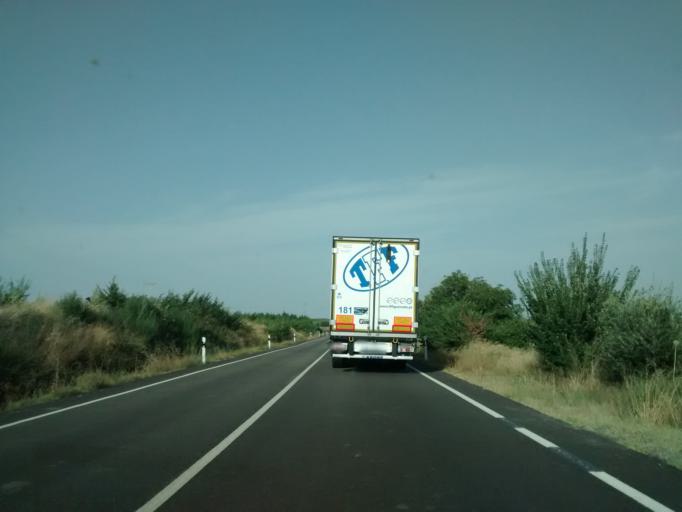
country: ES
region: Aragon
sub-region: Provincia de Zaragoza
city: Malejan
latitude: 41.8290
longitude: -1.5696
